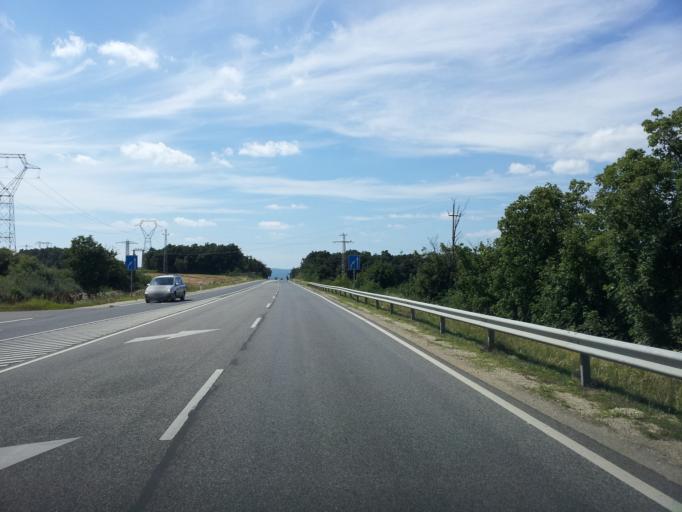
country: HU
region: Veszprem
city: Liter
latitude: 47.1090
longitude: 17.9957
